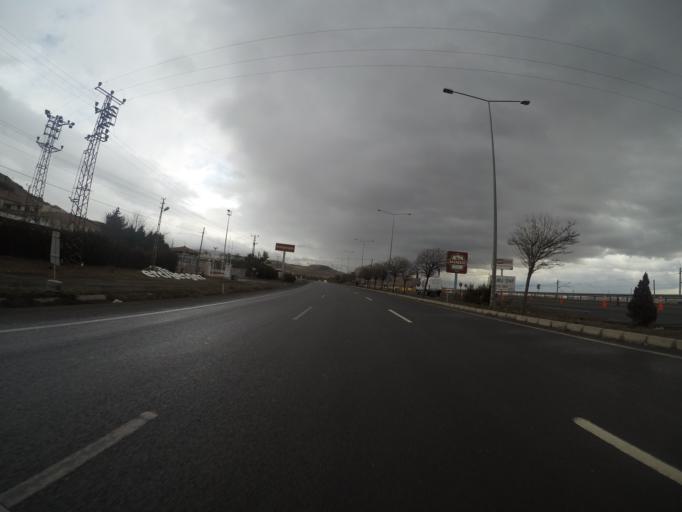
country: TR
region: Kayseri
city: Melikgazi
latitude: 38.7484
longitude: 35.3061
